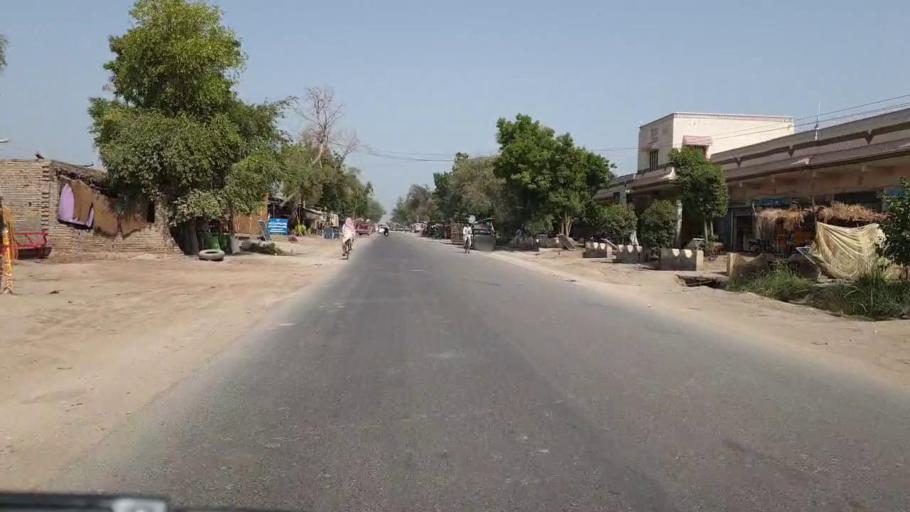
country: PK
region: Sindh
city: Sakrand
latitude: 26.2747
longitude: 68.1529
